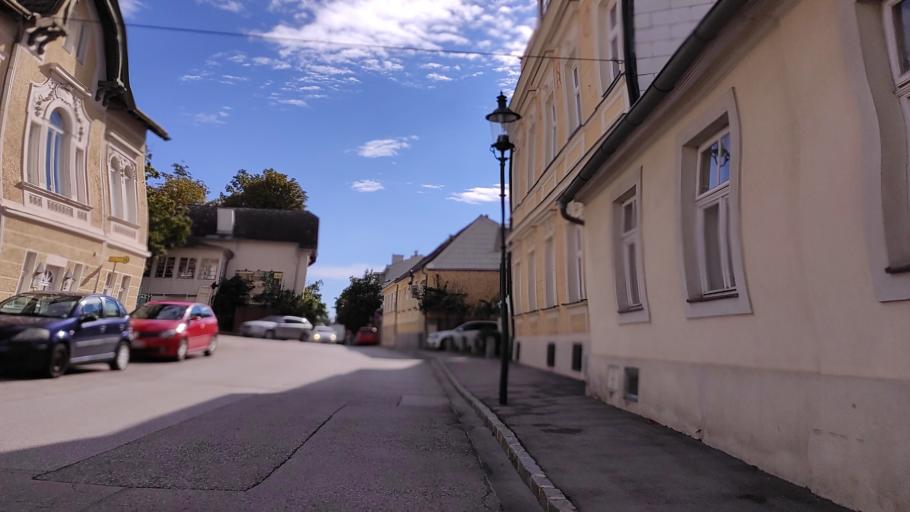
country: AT
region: Lower Austria
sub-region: Politischer Bezirk Baden
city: Baden
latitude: 48.0096
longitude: 16.2261
